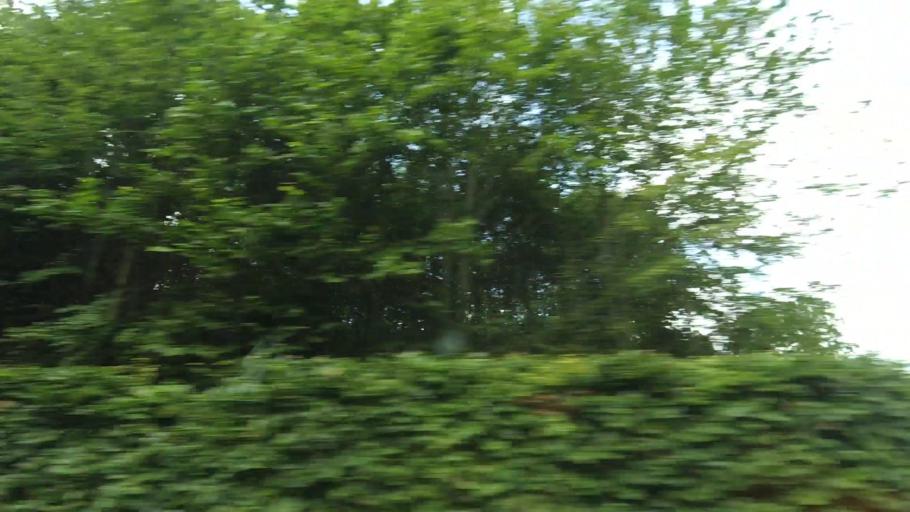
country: DK
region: Central Jutland
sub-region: Syddjurs Kommune
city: Ryomgard
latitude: 56.4413
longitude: 10.5599
